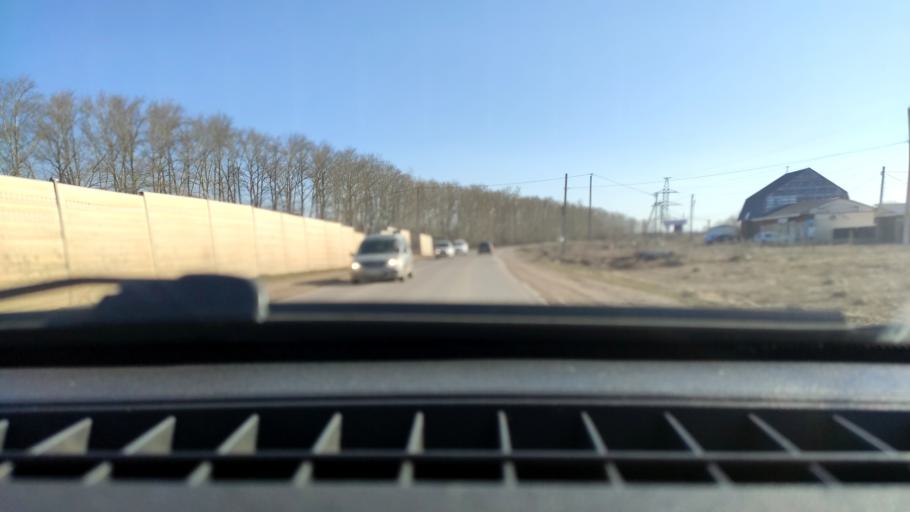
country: RU
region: Bashkortostan
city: Ufa
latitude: 54.6768
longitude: 56.0967
